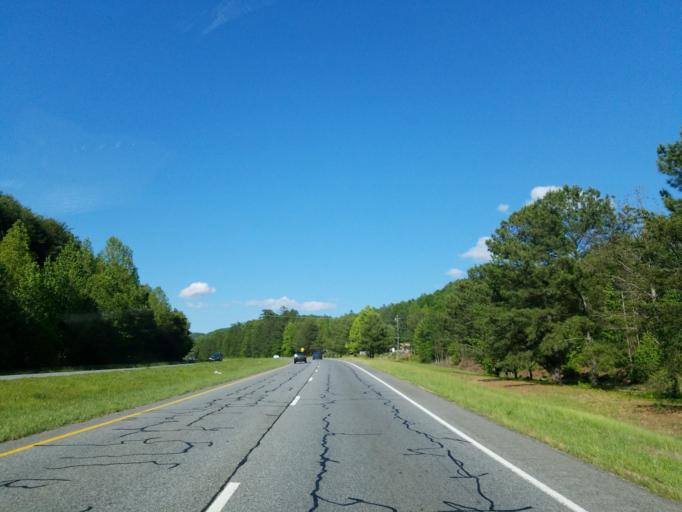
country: US
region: Georgia
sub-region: Gilmer County
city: Ellijay
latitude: 34.7427
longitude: -84.4152
